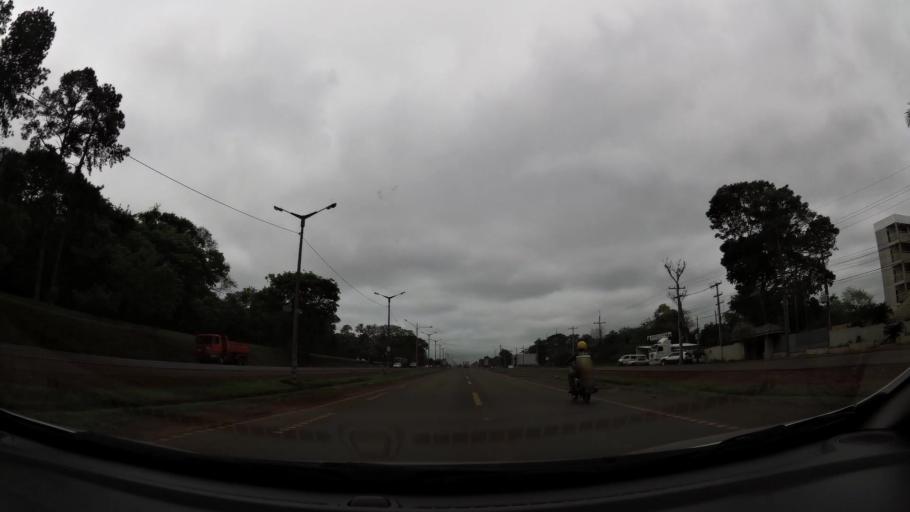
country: PY
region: Alto Parana
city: Ciudad del Este
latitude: -25.4951
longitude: -54.6978
